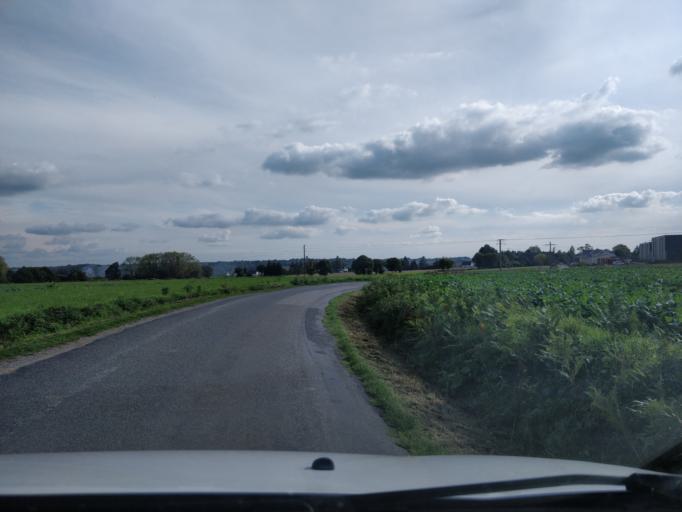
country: FR
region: Brittany
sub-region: Departement d'Ille-et-Vilaine
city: Chateaubourg
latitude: 48.1195
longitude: -1.3820
